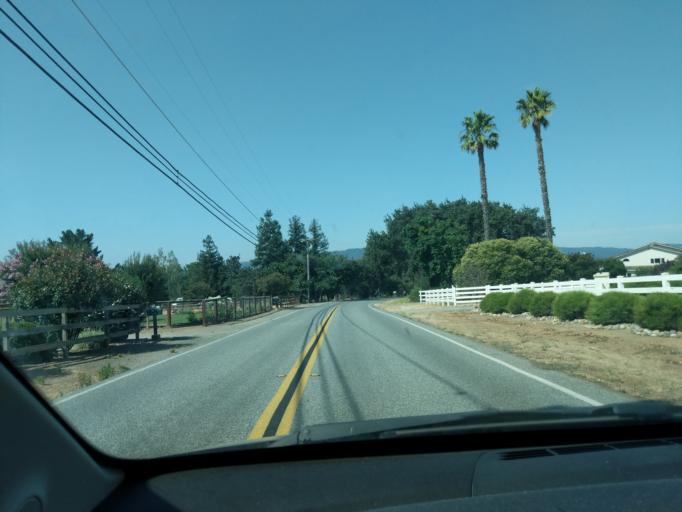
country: US
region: California
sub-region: Santa Clara County
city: Gilroy
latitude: 37.0446
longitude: -121.5353
